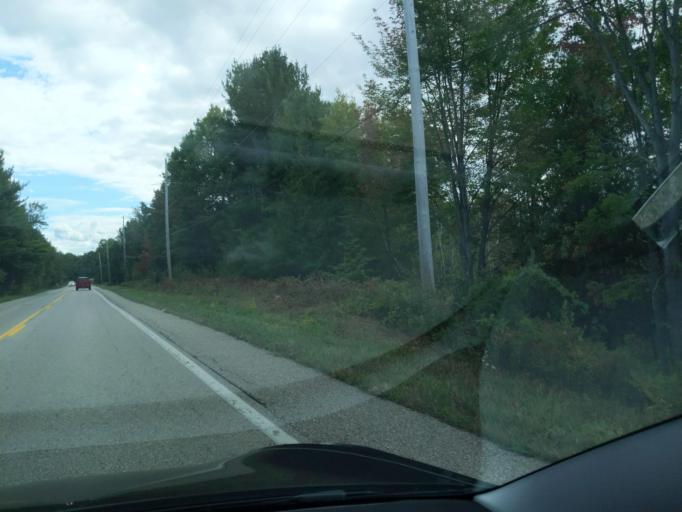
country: US
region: Michigan
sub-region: Kalkaska County
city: Rapid City
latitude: 44.9073
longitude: -85.2817
